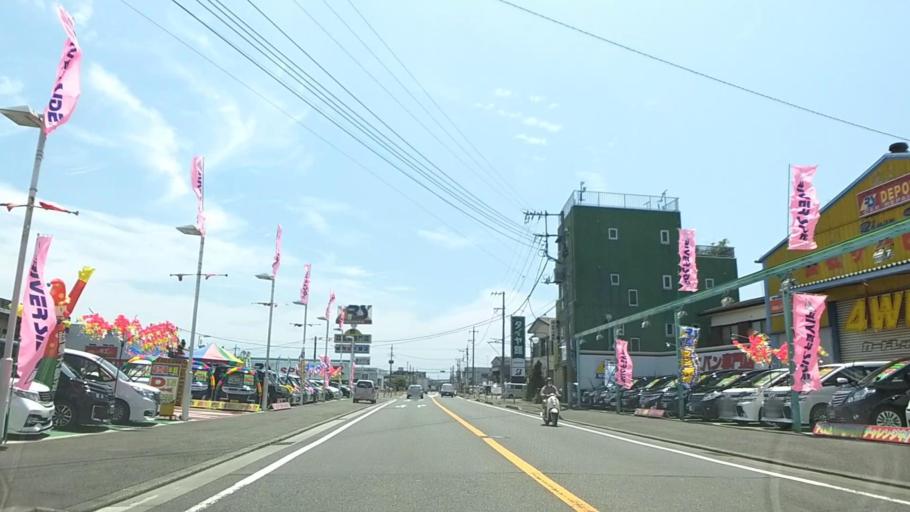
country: JP
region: Kanagawa
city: Atsugi
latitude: 35.4007
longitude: 139.3816
